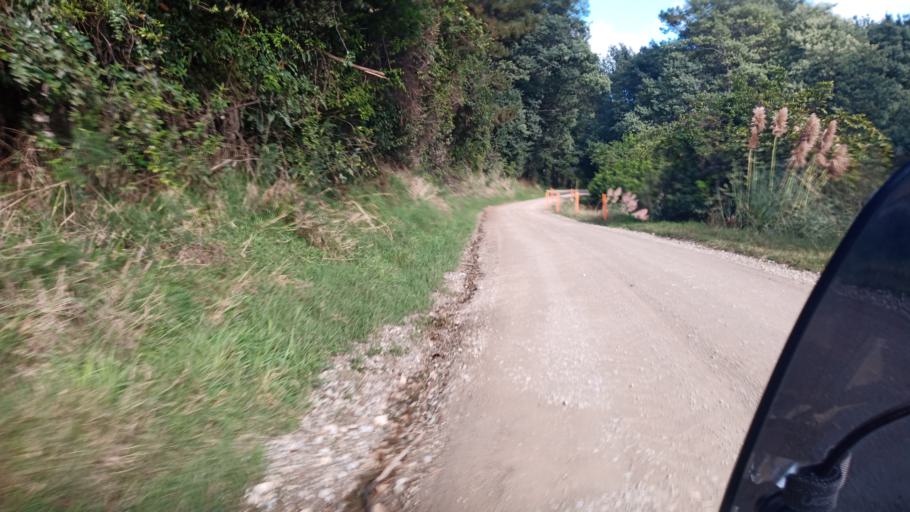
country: NZ
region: Gisborne
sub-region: Gisborne District
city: Gisborne
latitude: -38.5353
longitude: 177.5260
